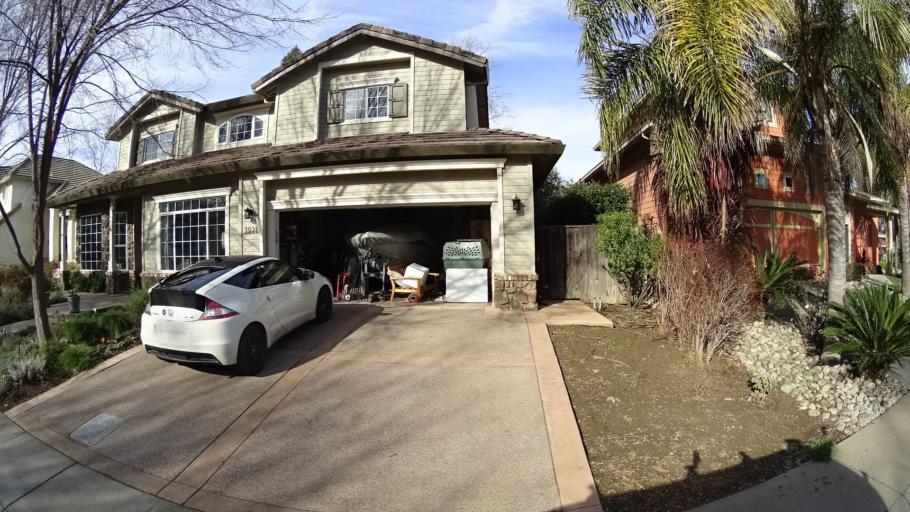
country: US
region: California
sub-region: Yolo County
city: Davis
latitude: 38.5461
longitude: -121.7044
